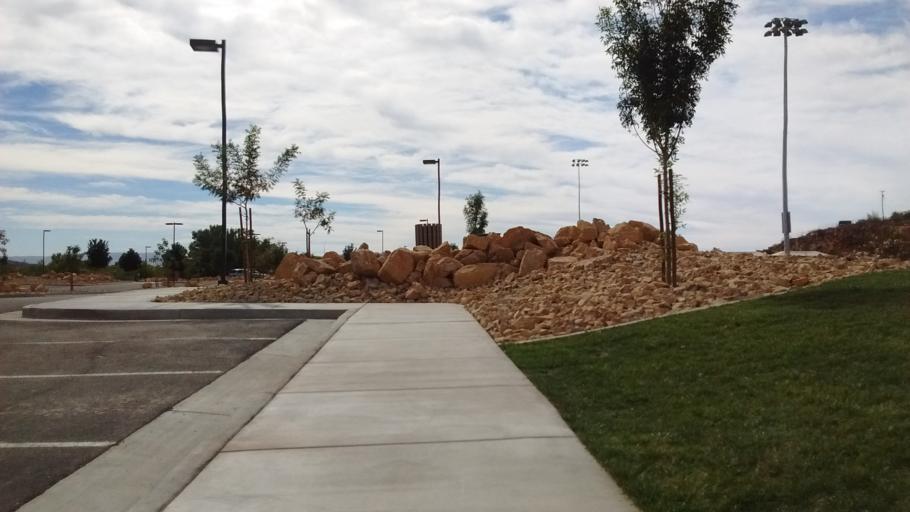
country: US
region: Utah
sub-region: Washington County
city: Washington
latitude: 37.1194
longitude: -113.5000
